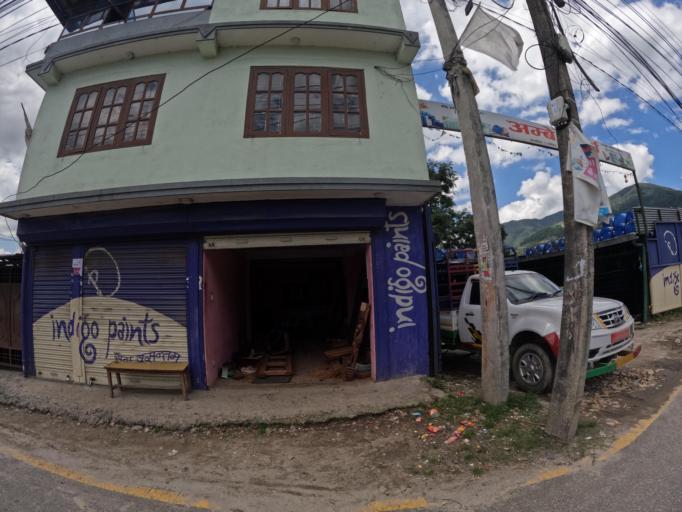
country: NP
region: Central Region
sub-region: Bagmati Zone
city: Kathmandu
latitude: 27.7799
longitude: 85.3252
